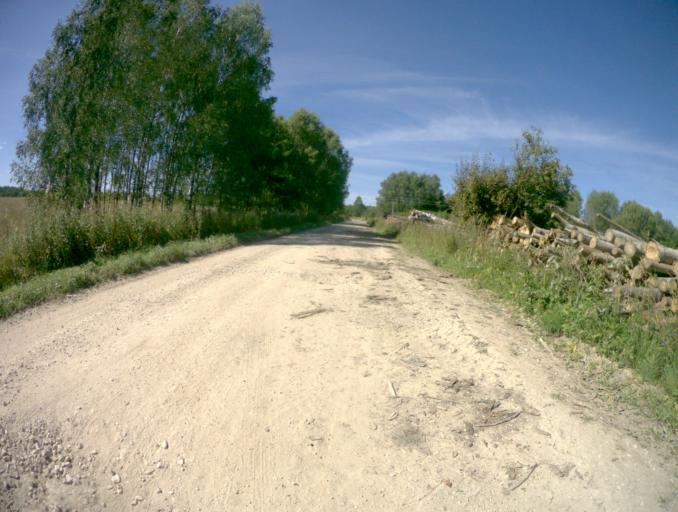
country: RU
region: Vladimir
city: Dobryatino
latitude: 55.6399
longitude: 41.2720
